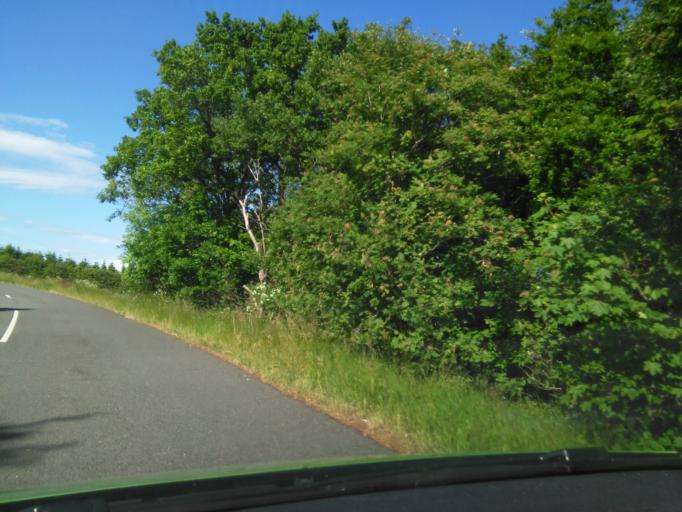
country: DK
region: Capital Region
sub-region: Bornholm Kommune
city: Nexo
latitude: 55.0666
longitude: 15.0832
